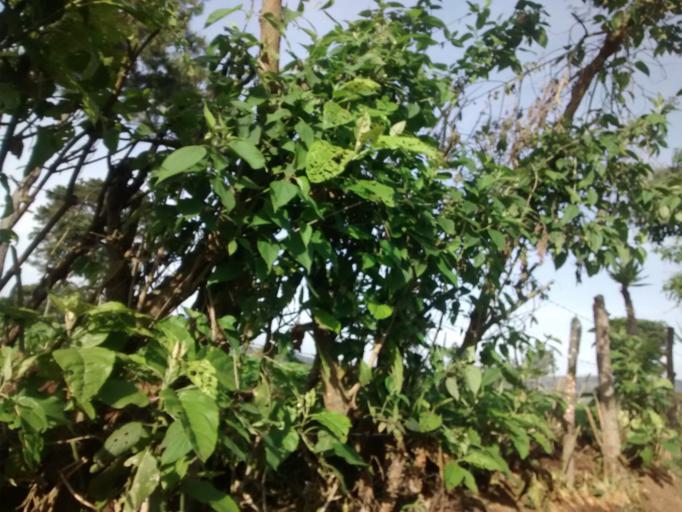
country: GT
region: Sacatepequez
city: Santo Domingo Xenacoj
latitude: 14.6866
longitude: -90.7204
